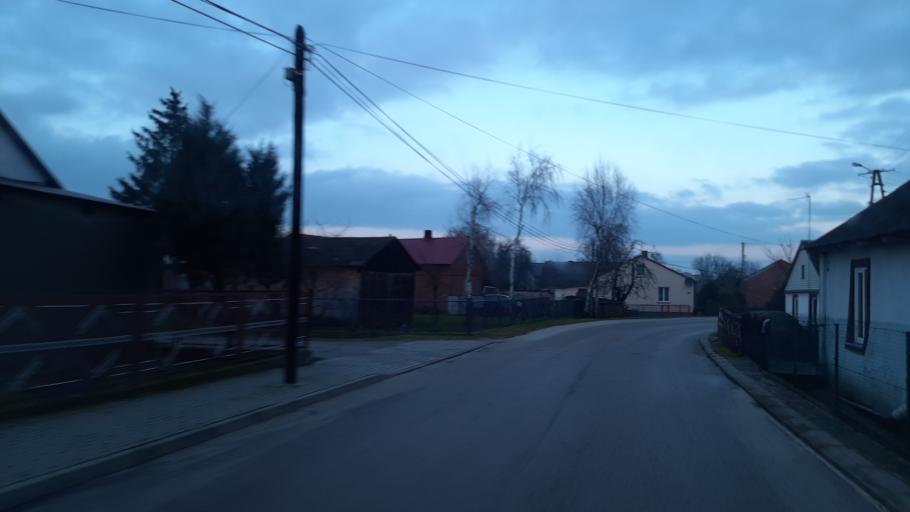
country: PL
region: Lublin Voivodeship
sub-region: Powiat lubartowski
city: Firlej
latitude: 51.5701
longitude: 22.5345
